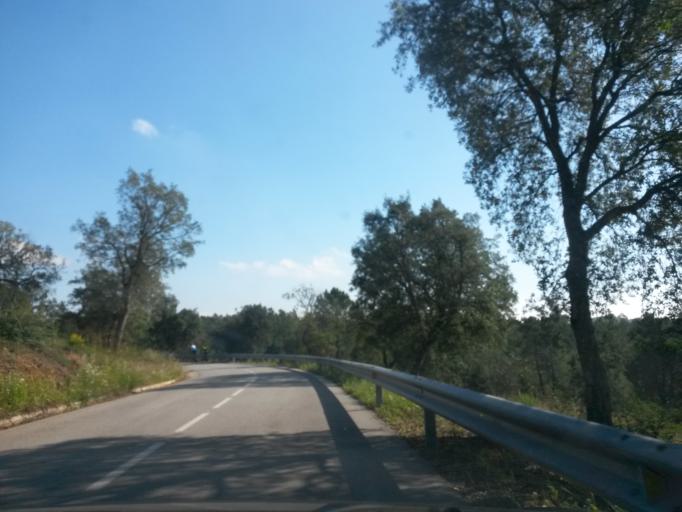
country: ES
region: Catalonia
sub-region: Provincia de Girona
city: Bescano
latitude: 41.9516
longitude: 2.6944
